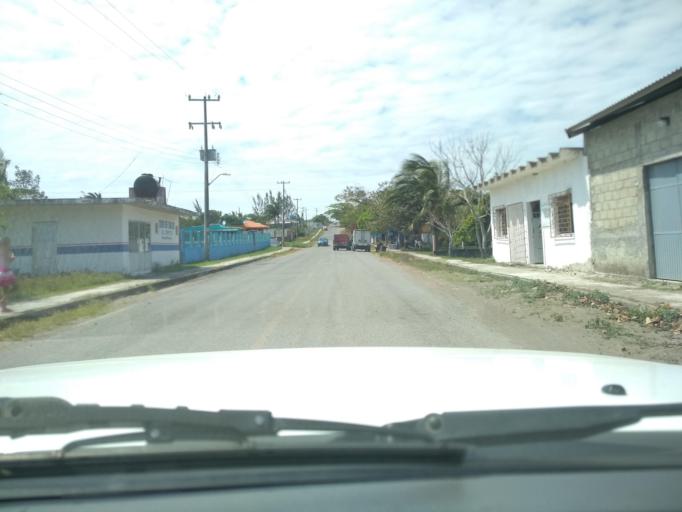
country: MX
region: Veracruz
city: Anton Lizardo
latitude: 19.0042
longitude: -95.9910
